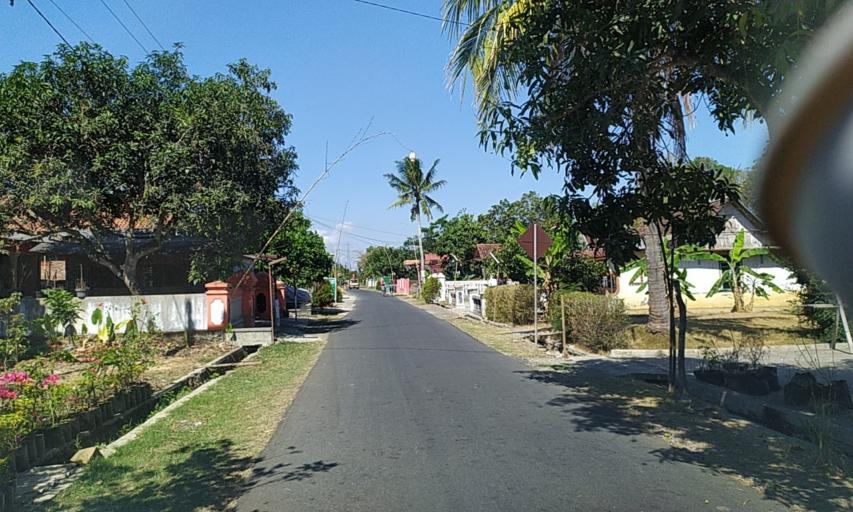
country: ID
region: Central Java
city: Mernek
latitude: -7.6142
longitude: 109.1860
